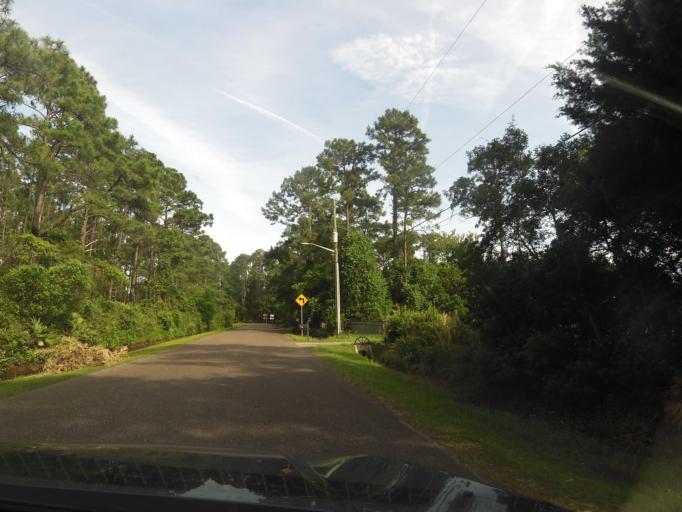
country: US
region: Florida
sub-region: Nassau County
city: Fernandina Beach
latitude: 30.5106
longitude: -81.4804
